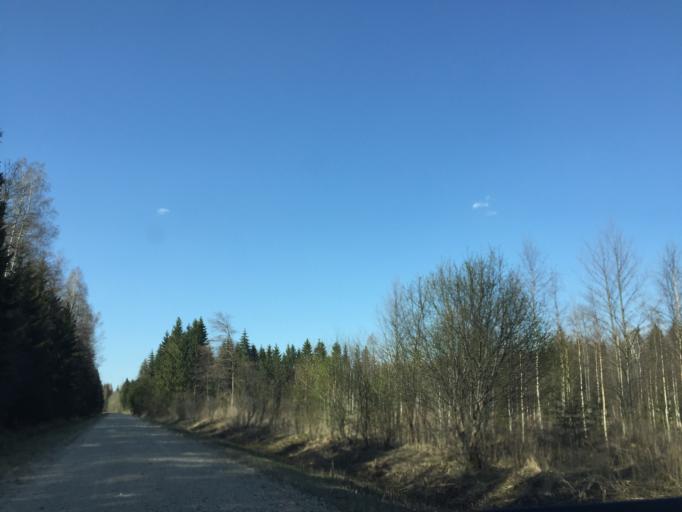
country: LV
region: Kegums
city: Kegums
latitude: 56.8762
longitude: 24.8001
